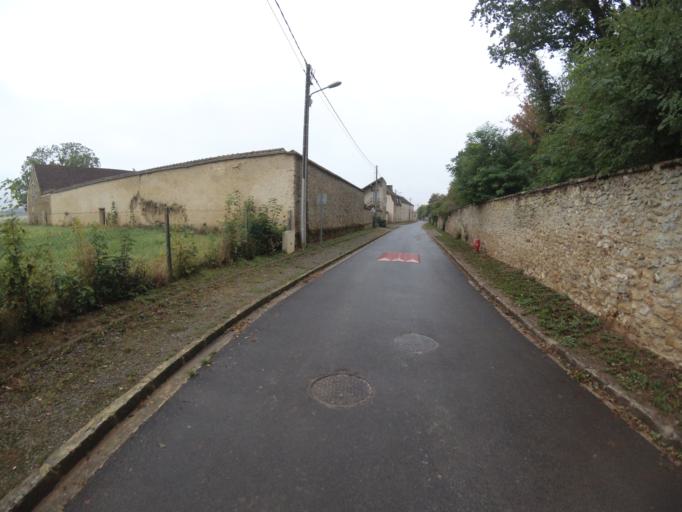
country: FR
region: Ile-de-France
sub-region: Departement de Seine-et-Marne
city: Chanteloup-en-Brie
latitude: 48.8362
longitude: 2.7558
